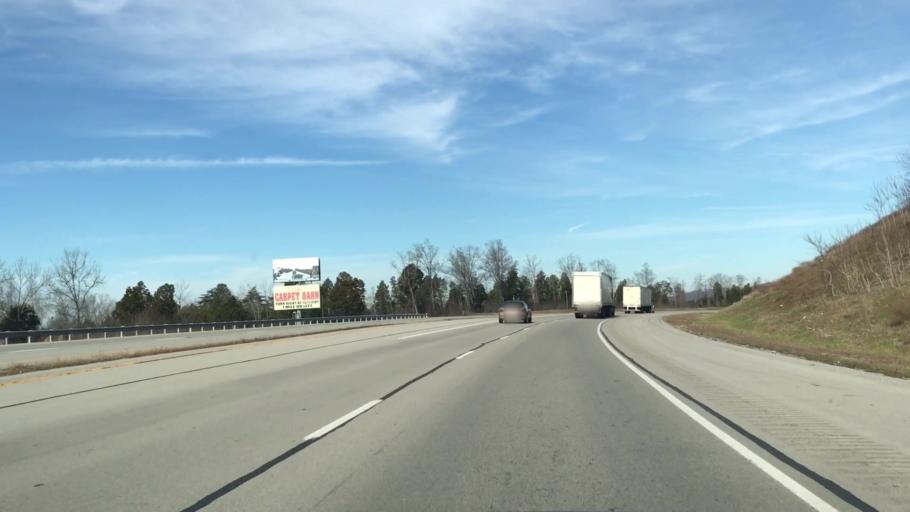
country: US
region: Kentucky
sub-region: Pulaski County
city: Somerset
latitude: 37.0134
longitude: -84.6006
